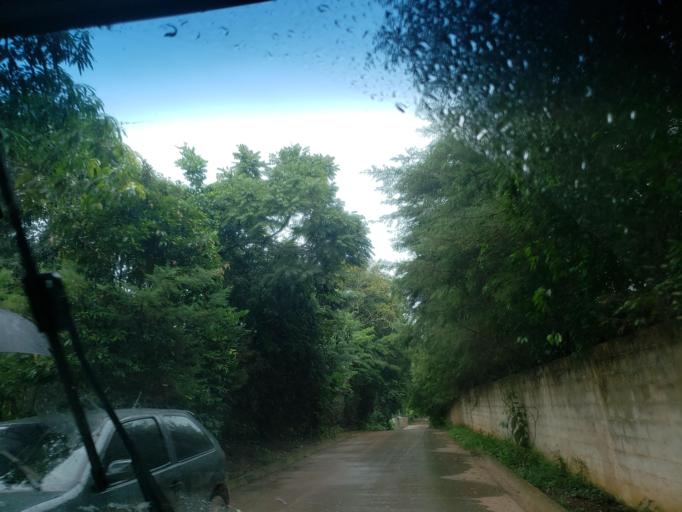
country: BR
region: Minas Gerais
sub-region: Monte Siao
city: Monte Siao
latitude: -22.3796
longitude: -46.5575
